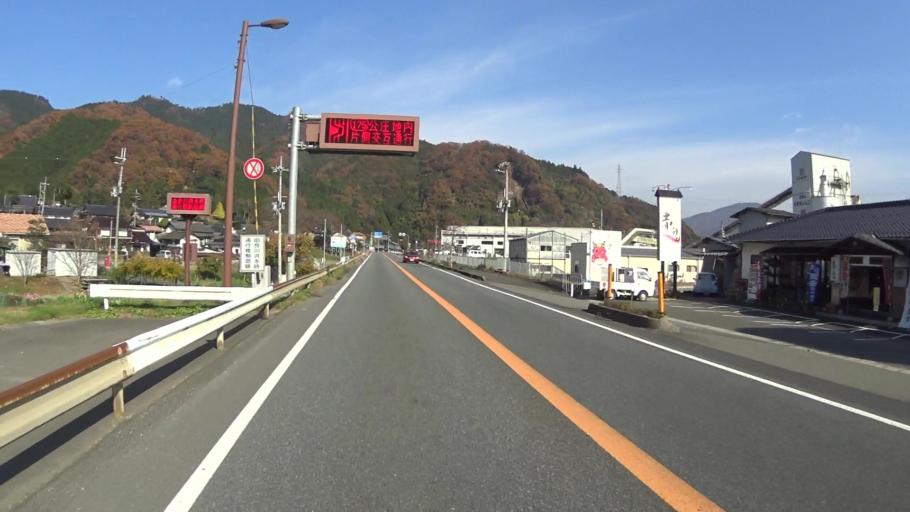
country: JP
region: Kyoto
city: Fukuchiyama
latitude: 35.3358
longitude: 135.0983
